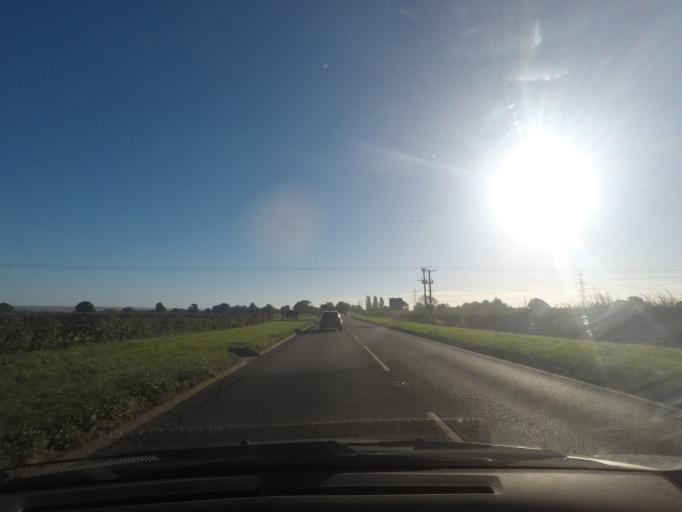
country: GB
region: England
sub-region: City of York
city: Elvington
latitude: 53.9513
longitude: -0.9465
